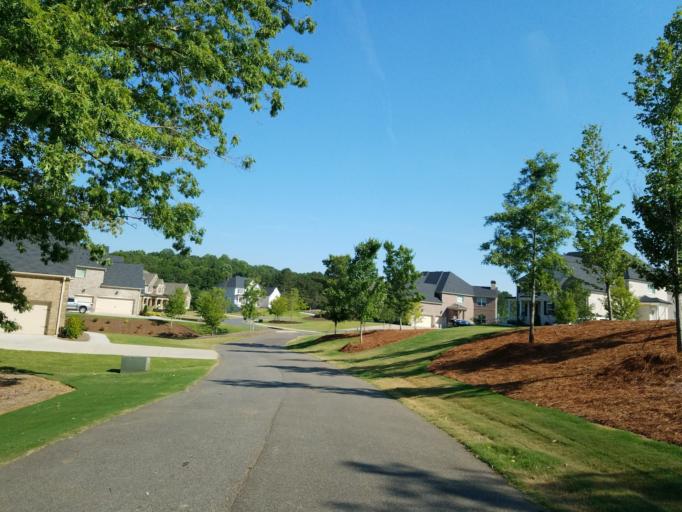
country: US
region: Georgia
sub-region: Fulton County
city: Milton
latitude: 34.1827
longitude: -84.3260
